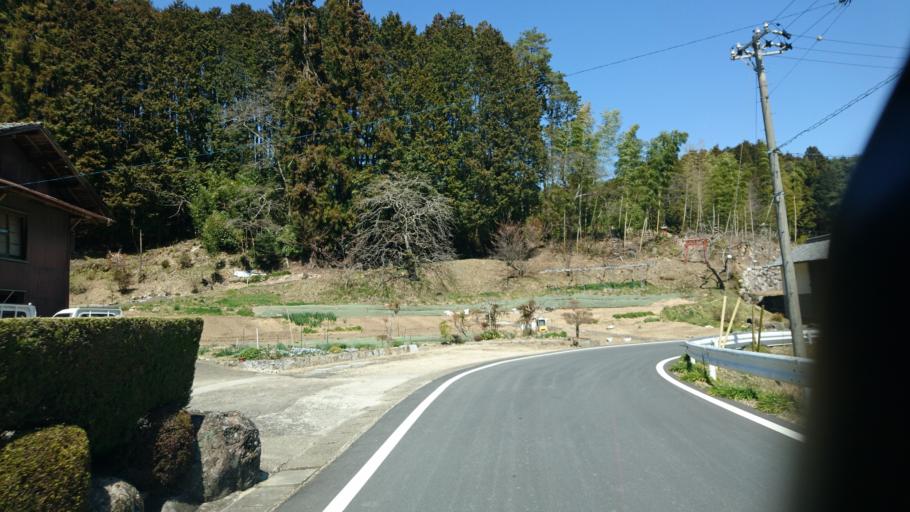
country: JP
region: Gifu
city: Mizunami
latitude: 35.4609
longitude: 137.3445
